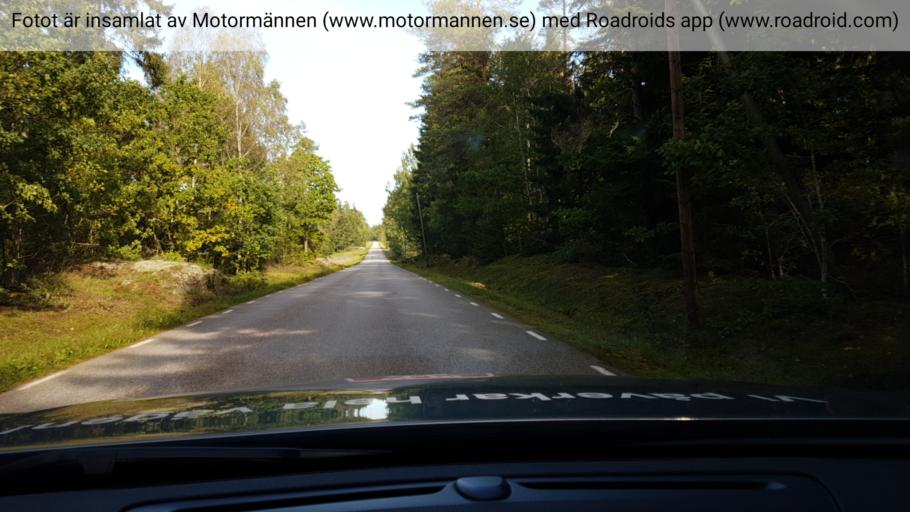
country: SE
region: OEstergoetland
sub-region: Valdemarsviks Kommun
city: Valdemarsvik
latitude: 58.0478
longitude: 16.6054
